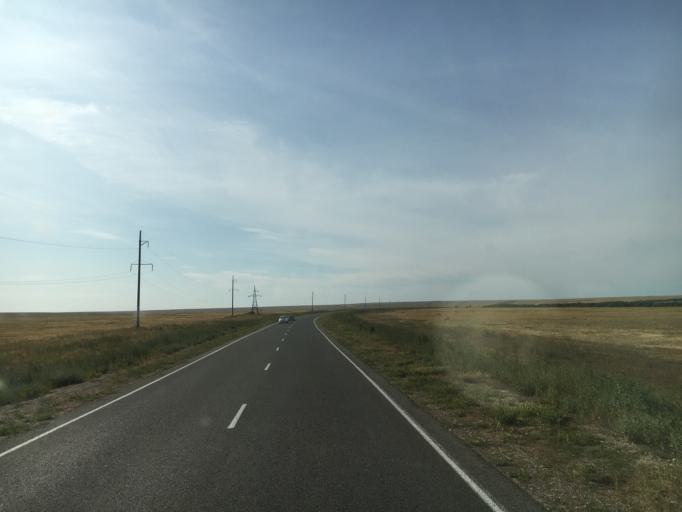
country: KZ
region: Batys Qazaqstan
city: Kamenka
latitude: 51.1460
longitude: 50.0893
